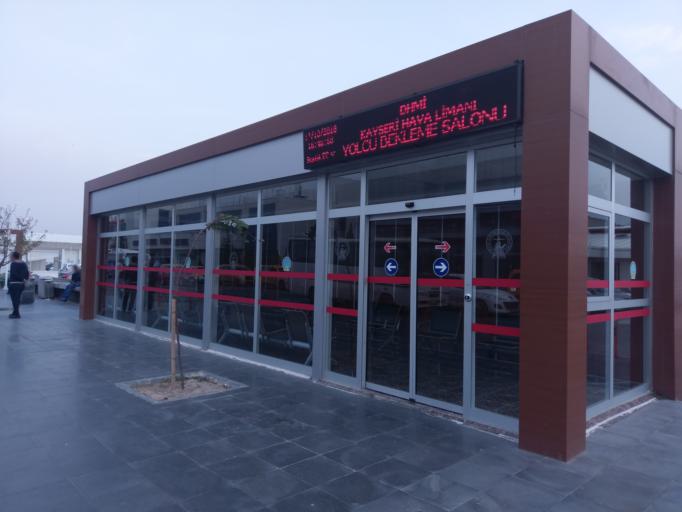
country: TR
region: Kayseri
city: Kayseri
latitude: 38.7650
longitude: 35.4819
